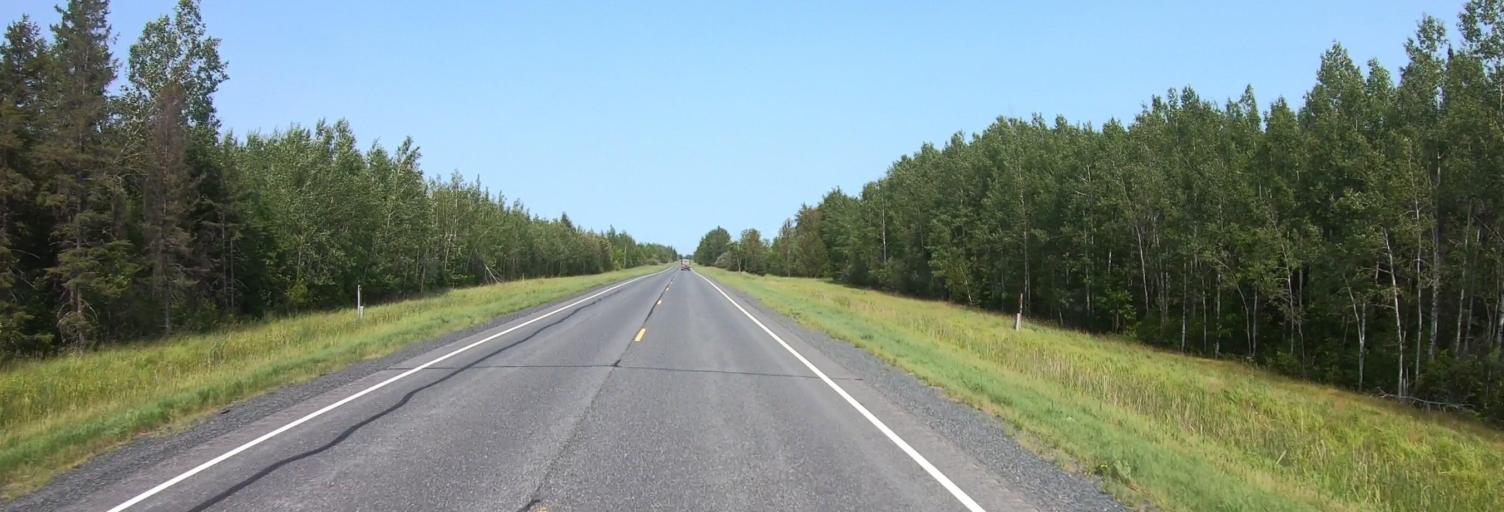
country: US
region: Minnesota
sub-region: Koochiching County
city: International Falls
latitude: 48.5641
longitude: -93.8180
